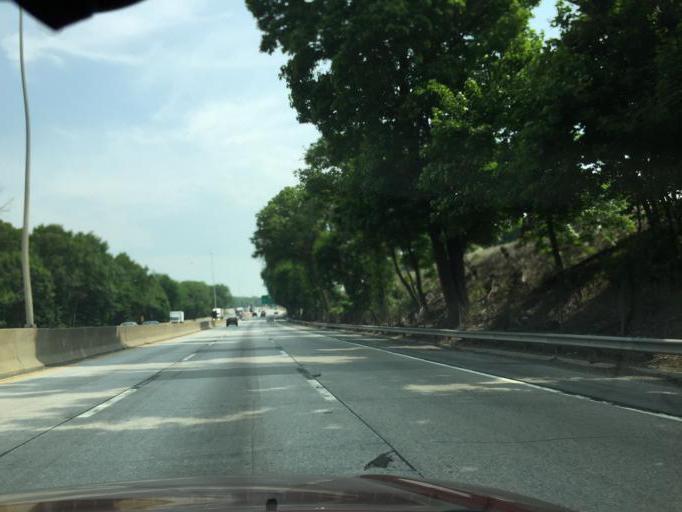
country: US
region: New York
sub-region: Westchester County
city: Pelham Manor
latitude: 40.8943
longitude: -73.7986
